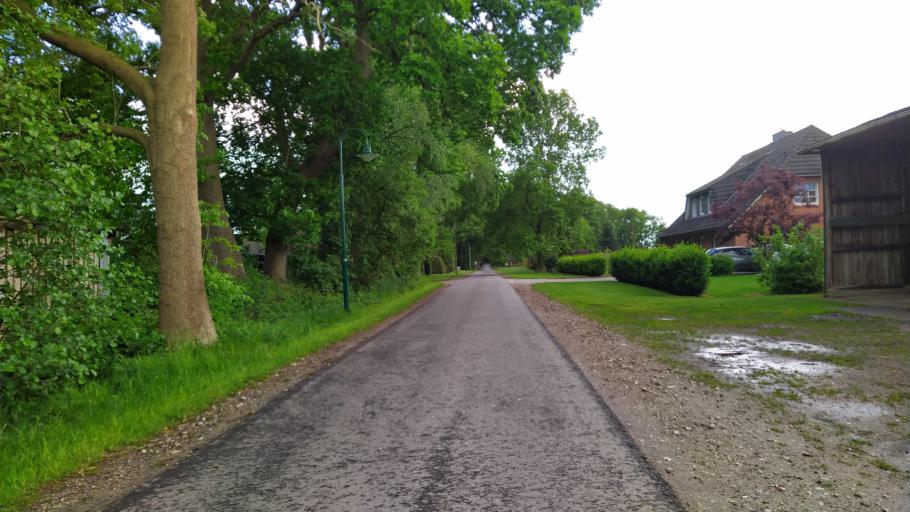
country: DE
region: Lower Saxony
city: Brest
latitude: 53.4500
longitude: 9.3793
